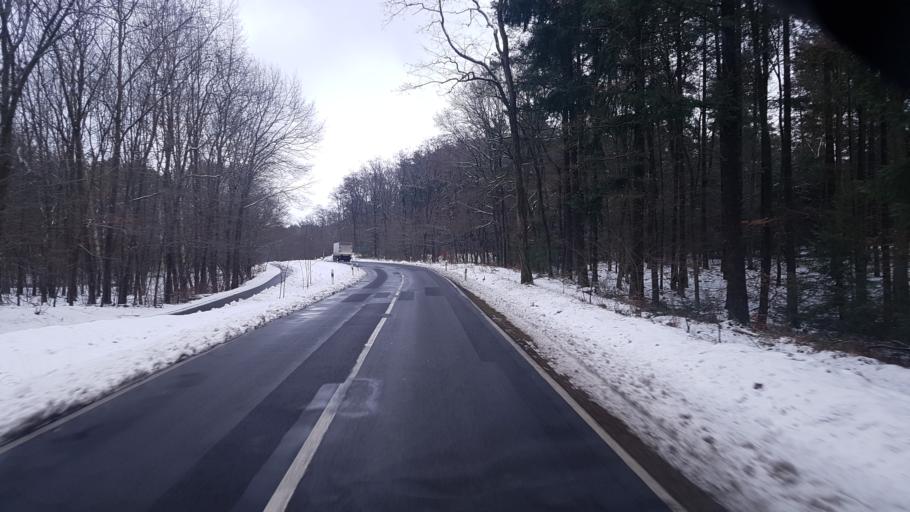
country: DE
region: Brandenburg
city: Lawitz
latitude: 52.0831
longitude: 14.5076
